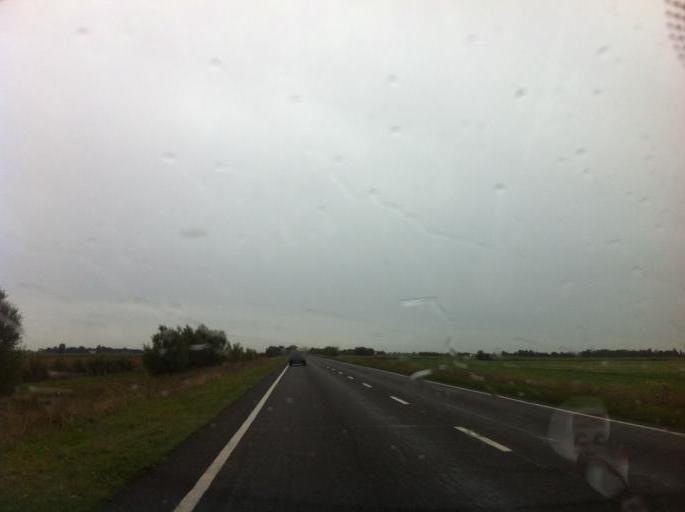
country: GB
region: England
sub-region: Peterborough
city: Eye
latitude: 52.6224
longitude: -0.2056
